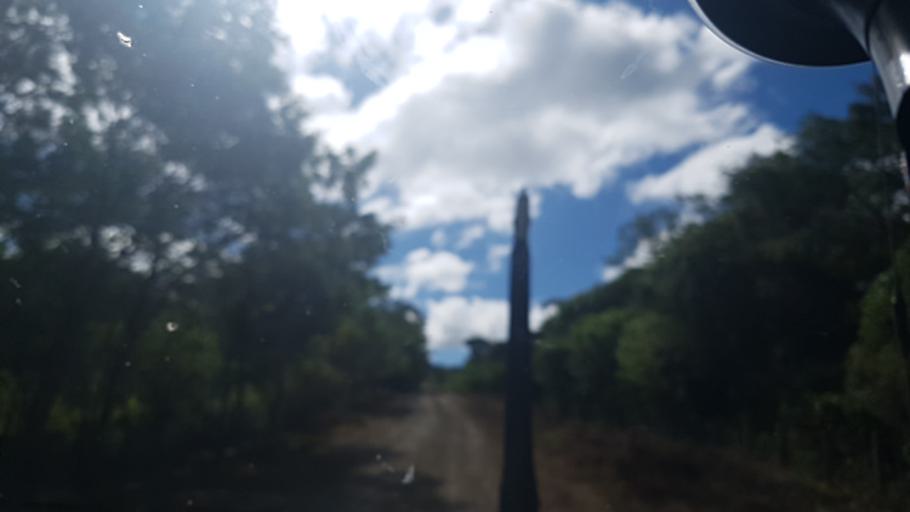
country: NI
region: Carazo
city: Santa Teresa
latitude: 11.6302
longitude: -86.1668
